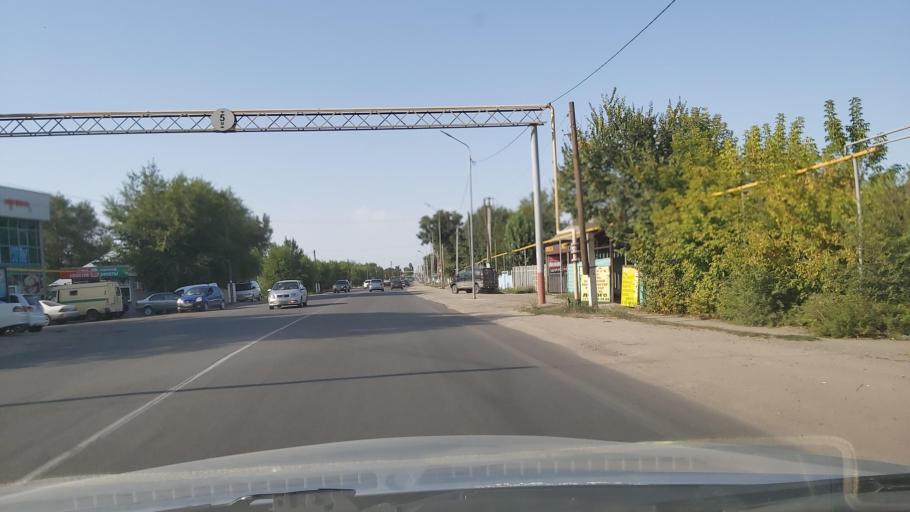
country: KZ
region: Almaty Oblysy
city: Energeticheskiy
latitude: 43.4857
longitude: 77.0342
